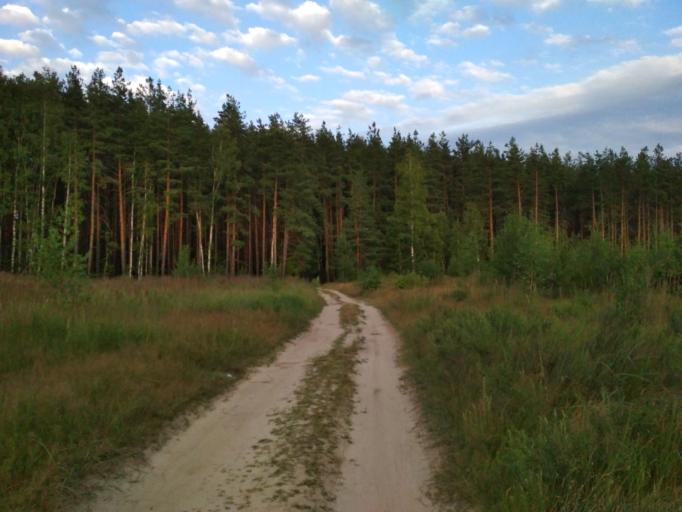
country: RU
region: Rjazan
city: Solotcha
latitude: 54.8302
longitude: 39.9452
